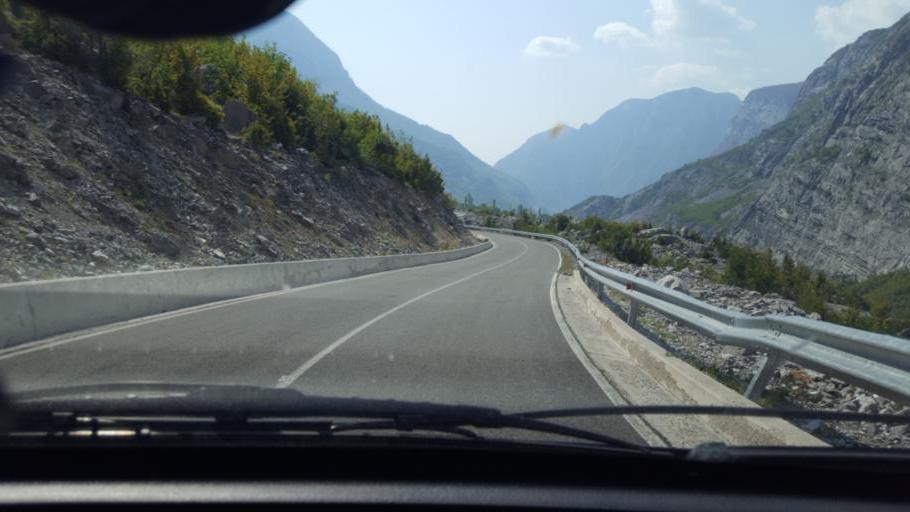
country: AL
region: Shkoder
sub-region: Rrethi i Malesia e Madhe
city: Kastrat
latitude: 42.5203
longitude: 19.6283
